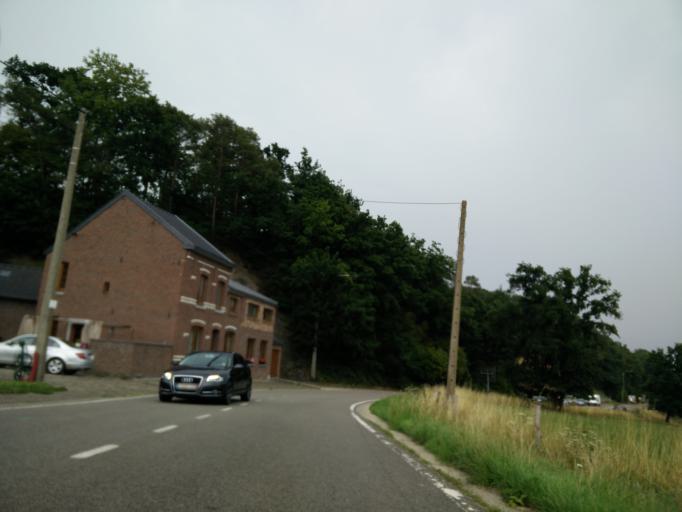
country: BE
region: Wallonia
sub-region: Province de Liege
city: Dalhem
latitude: 50.7174
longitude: 5.7498
